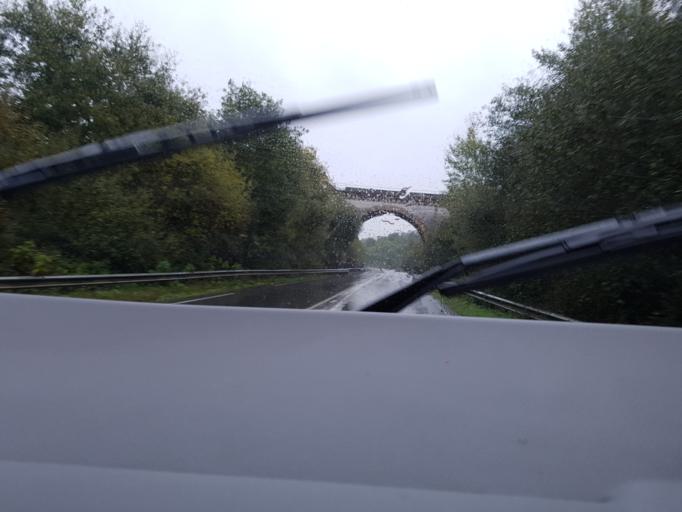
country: FR
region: Aquitaine
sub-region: Departement de la Gironde
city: Saint-Vincent-de-Paul
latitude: 44.9593
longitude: -0.4801
